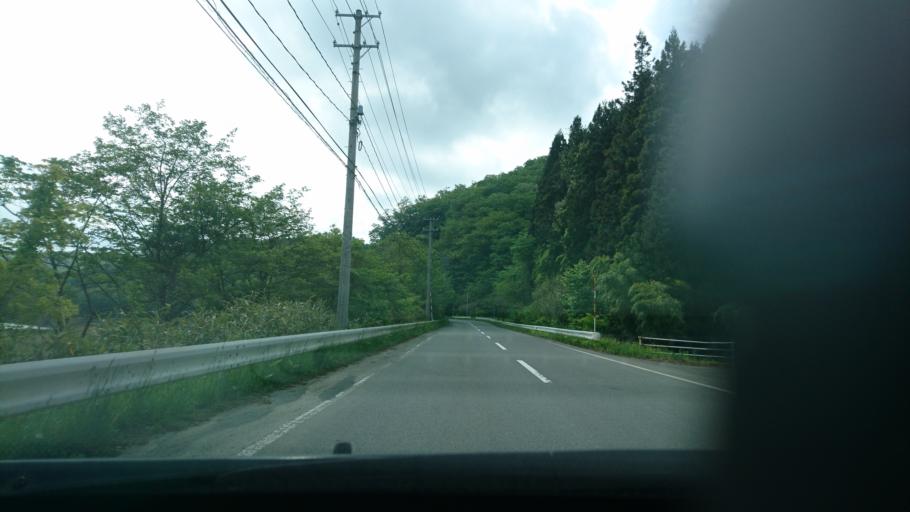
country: JP
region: Iwate
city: Ichinoseki
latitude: 38.9055
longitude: 140.8990
